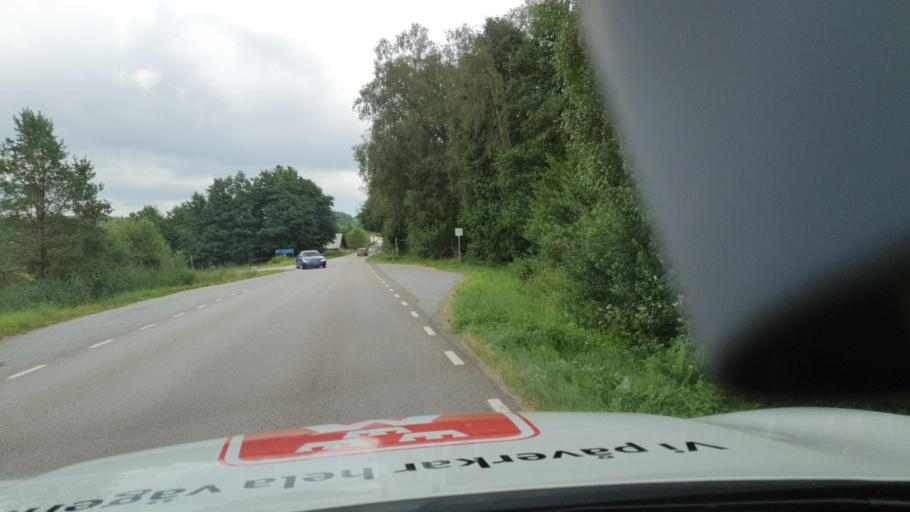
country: SE
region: Vaestra Goetaland
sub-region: Tanums Kommun
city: Grebbestad
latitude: 58.6717
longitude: 11.2930
